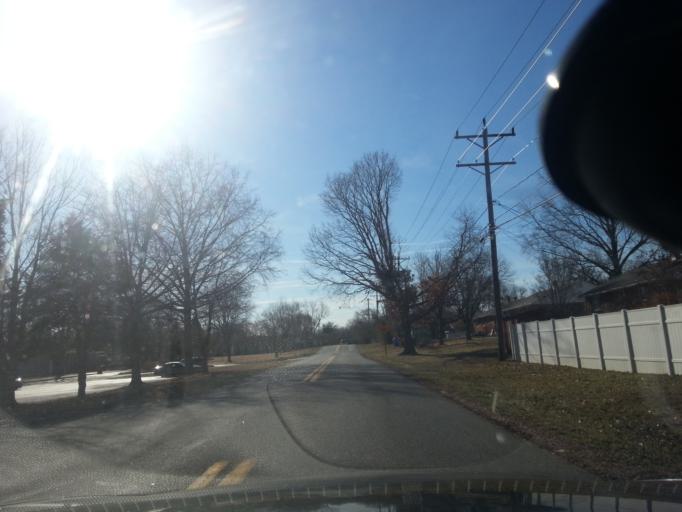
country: US
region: Delaware
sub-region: New Castle County
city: Brookside
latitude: 39.6707
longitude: -75.7135
